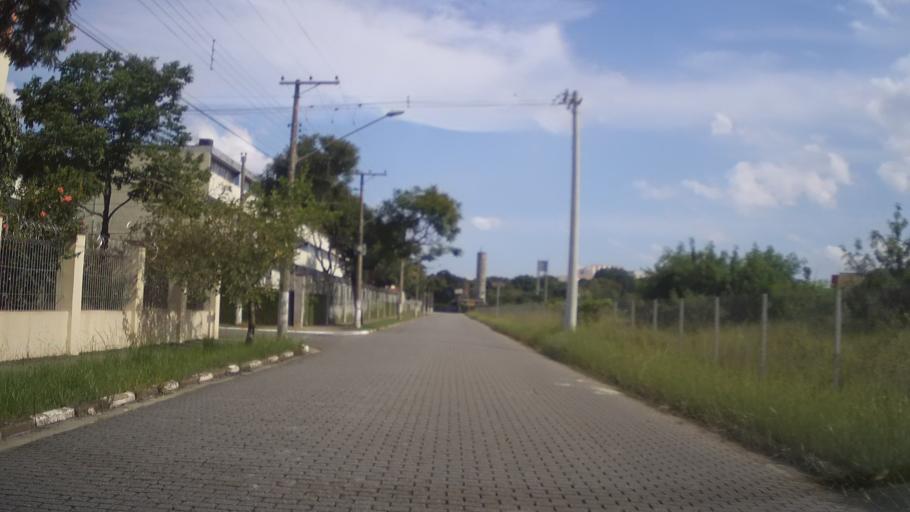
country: BR
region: Sao Paulo
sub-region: Guarulhos
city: Guarulhos
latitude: -23.4517
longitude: -46.5001
